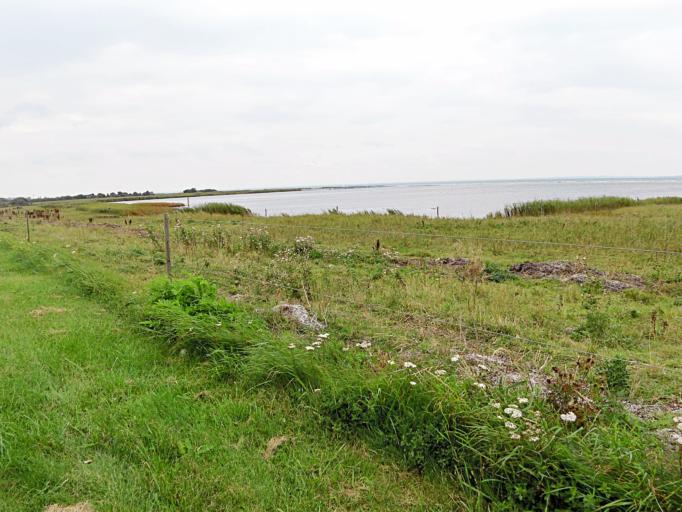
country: DK
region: Capital Region
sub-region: Fredensborg Kommune
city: Niva
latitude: 55.9256
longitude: 12.5179
